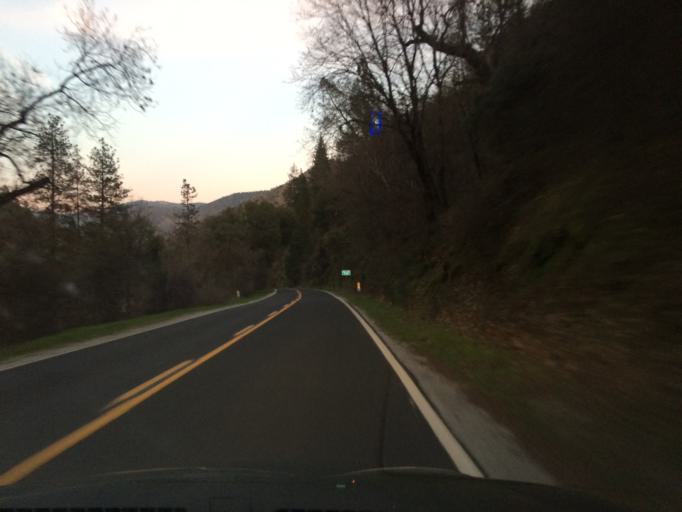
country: US
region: California
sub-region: Mariposa County
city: Midpines
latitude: 37.6698
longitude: -119.8252
